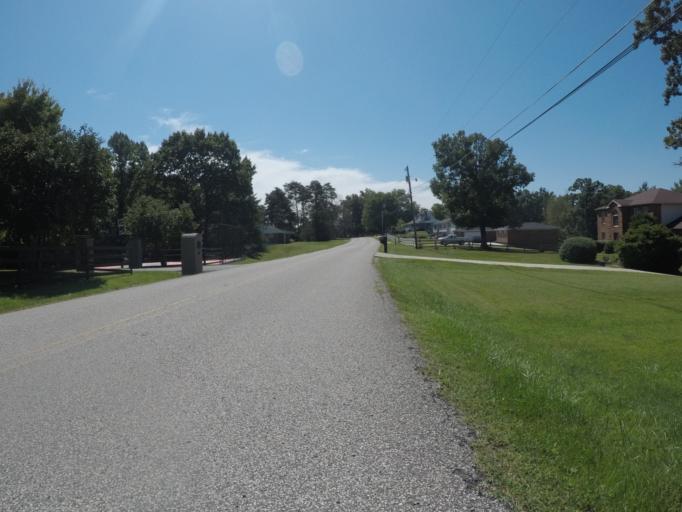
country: US
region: Kentucky
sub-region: Boyd County
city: Meads
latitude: 38.4133
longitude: -82.6583
